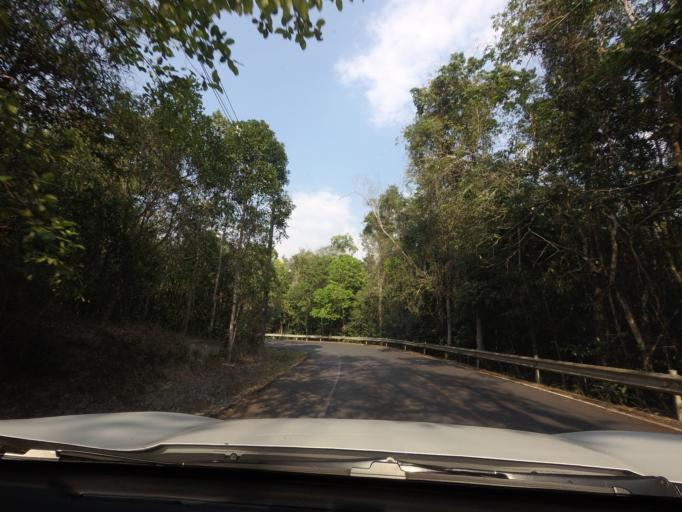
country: TH
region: Nakhon Ratchasima
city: Pak Chong
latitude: 14.4253
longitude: 101.3935
